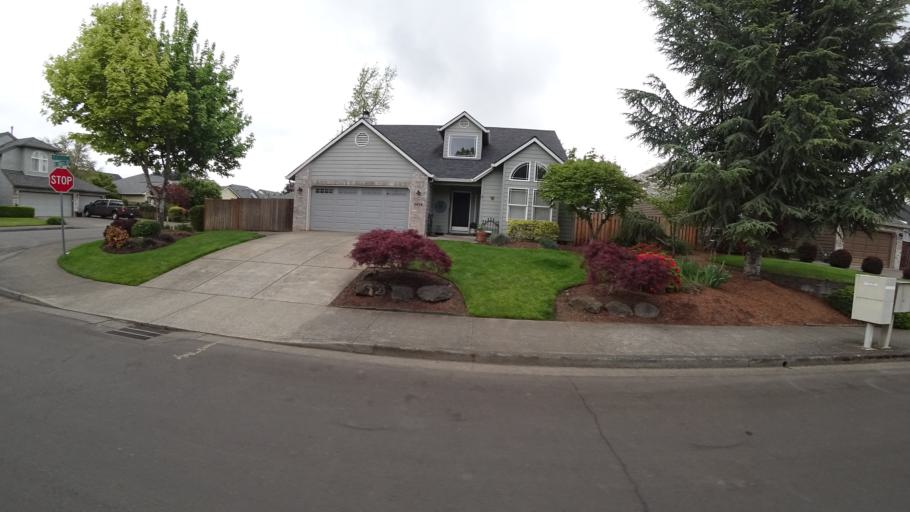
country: US
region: Oregon
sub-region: Washington County
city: Hillsboro
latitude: 45.5429
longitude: -122.9855
